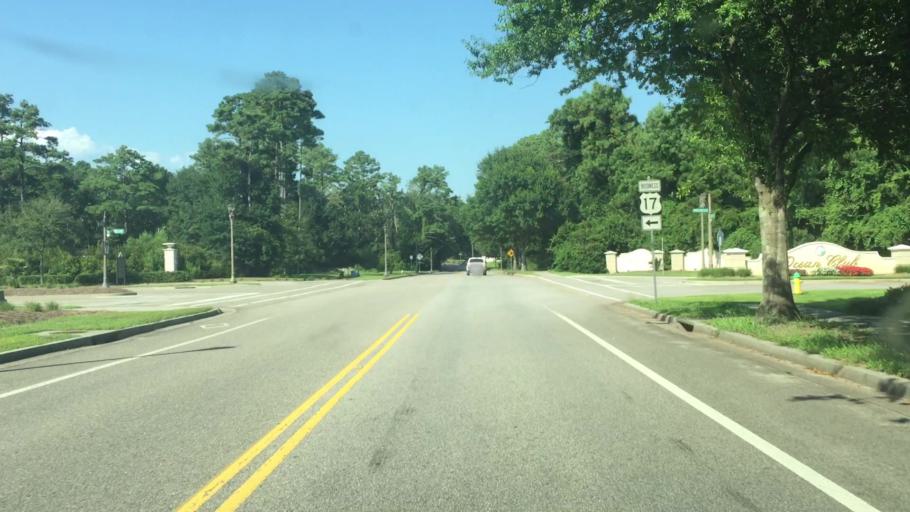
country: US
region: South Carolina
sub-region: Horry County
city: Myrtle Beach
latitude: 33.7509
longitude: -78.8085
